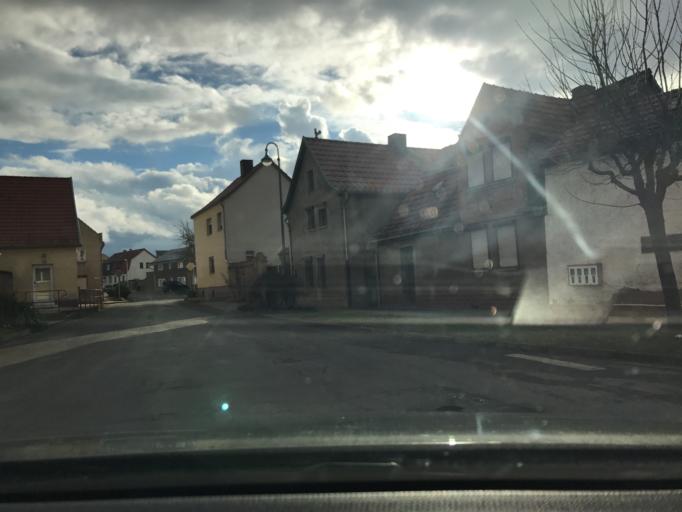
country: DE
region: Saxony-Anhalt
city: Wallhausen
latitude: 51.4448
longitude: 11.1961
